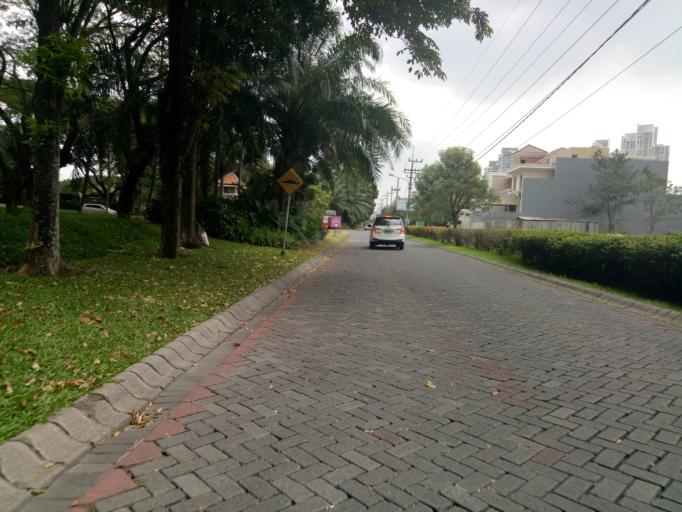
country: ID
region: East Java
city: Jagirsidosermo
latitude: -7.2917
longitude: 112.6869
